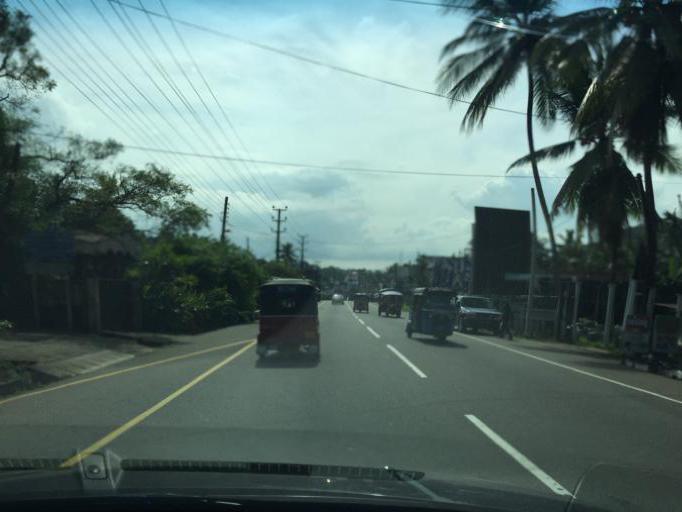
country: LK
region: Western
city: Horana South
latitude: 6.7199
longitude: 80.0720
